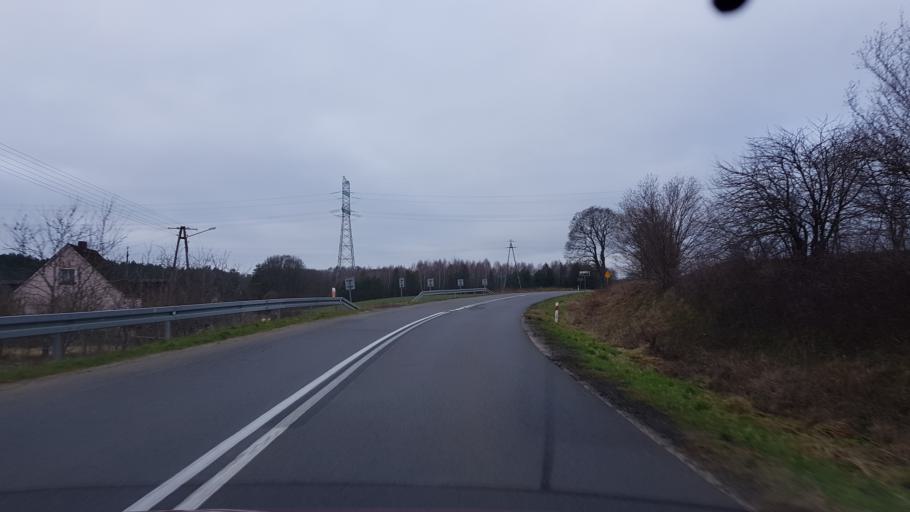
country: PL
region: Pomeranian Voivodeship
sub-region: Powiat slupski
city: Kepice
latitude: 54.2889
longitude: 16.9059
